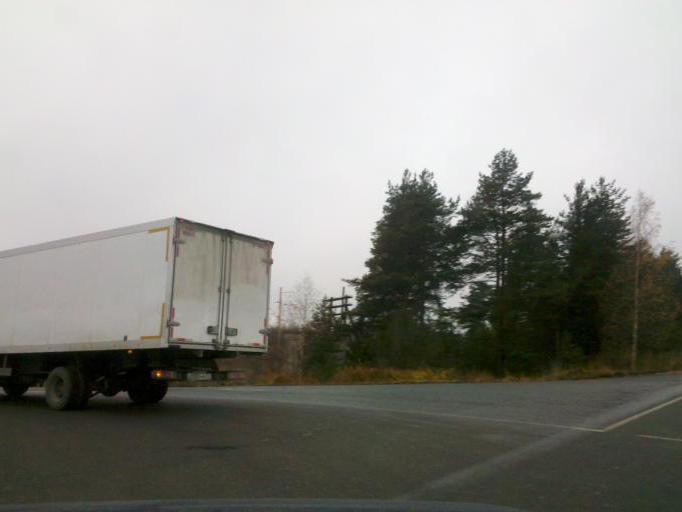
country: RU
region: Republic of Karelia
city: Petrozavodsk
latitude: 61.8236
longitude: 34.2658
